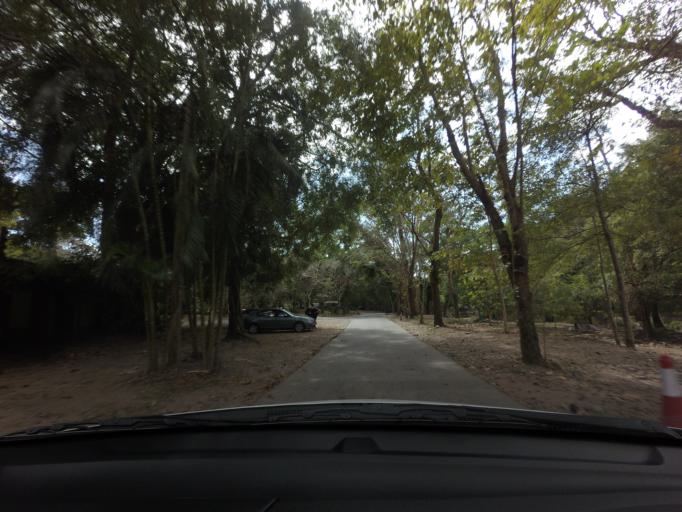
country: TH
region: Nakhon Nayok
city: Nakhon Nayok
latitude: 14.3325
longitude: 101.3055
